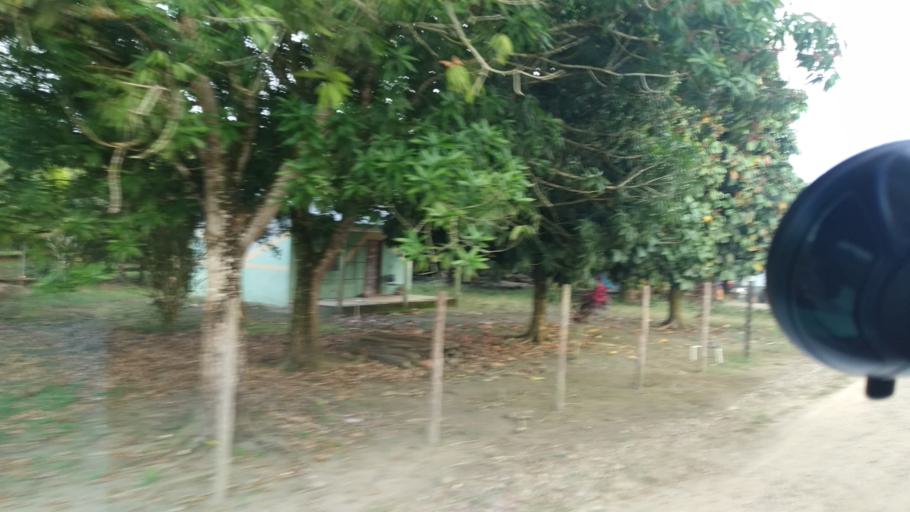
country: BZ
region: Stann Creek
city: Placencia
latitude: 16.5699
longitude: -88.5279
